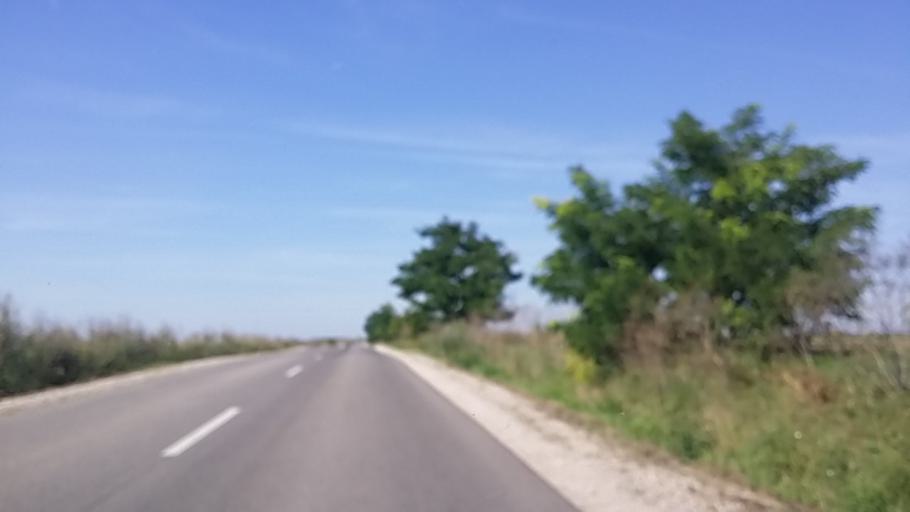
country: HU
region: Fejer
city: Pusztaszabolcs
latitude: 47.0987
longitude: 18.7125
